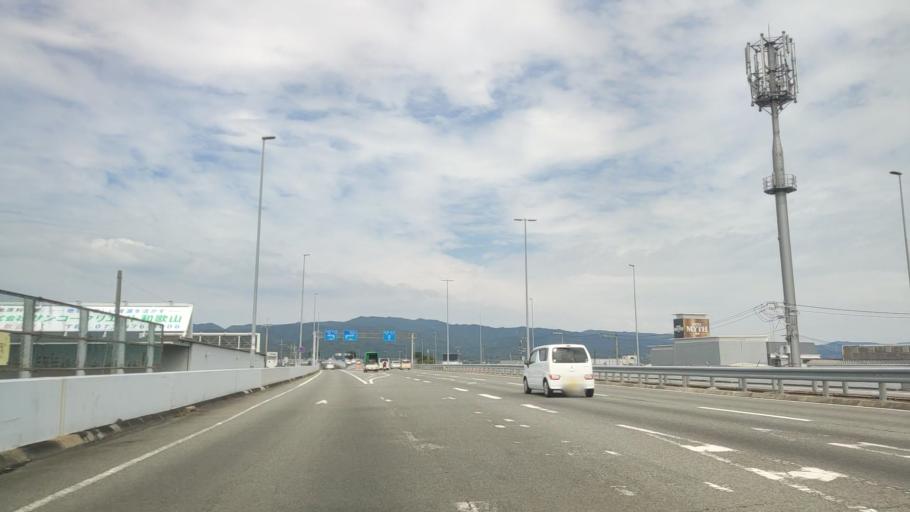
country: JP
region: Wakayama
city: Wakayama-shi
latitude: 34.2423
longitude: 135.2174
